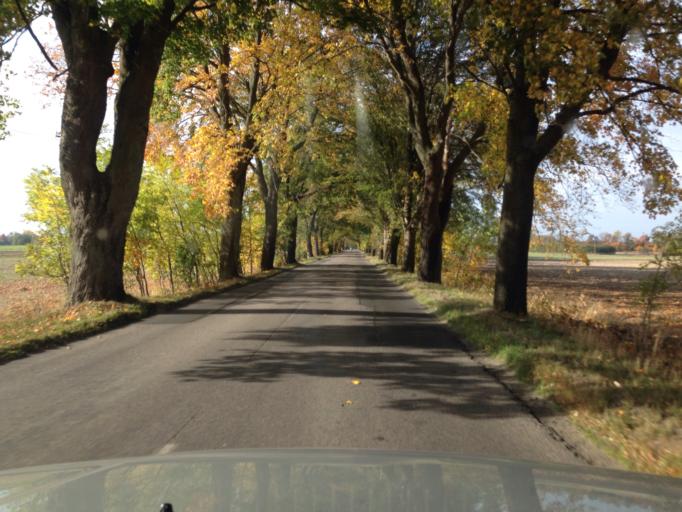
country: PL
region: Pomeranian Voivodeship
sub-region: Powiat koscierski
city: Stara Kiszewa
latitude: 54.0210
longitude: 18.1015
